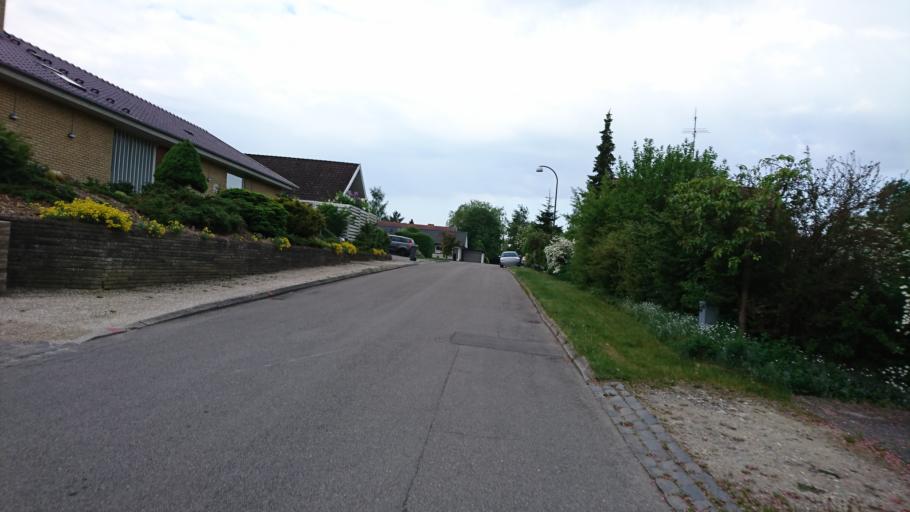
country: DK
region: Capital Region
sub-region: Fureso Kommune
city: Vaerlose
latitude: 55.7565
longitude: 12.3984
